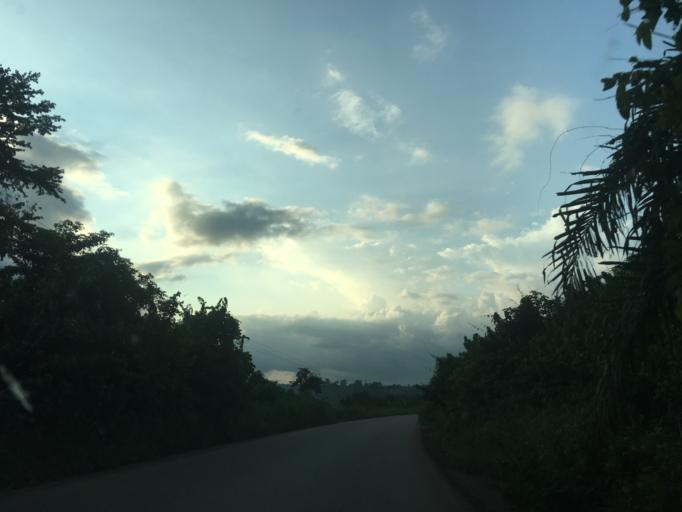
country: GH
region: Western
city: Bibiani
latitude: 6.6353
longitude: -2.4245
